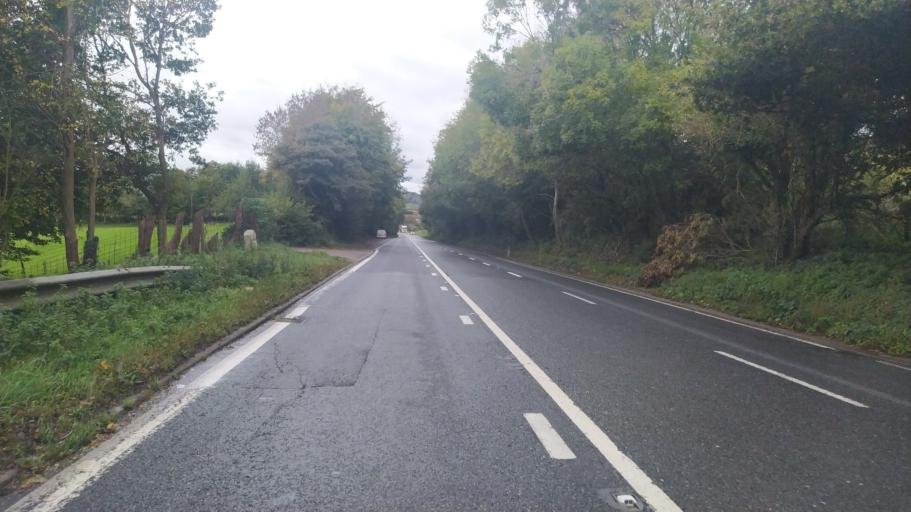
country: GB
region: England
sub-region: Dorset
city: Bridport
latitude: 50.7337
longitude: -2.7225
